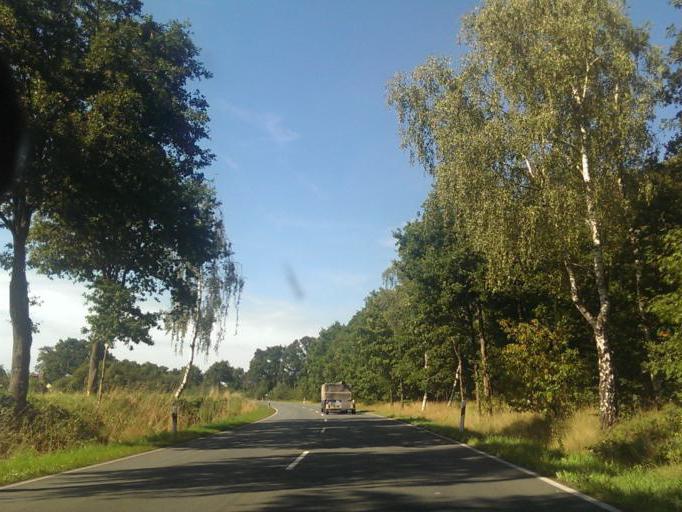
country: DE
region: North Rhine-Westphalia
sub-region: Regierungsbezirk Detmold
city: Hovelhof
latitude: 51.7906
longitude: 8.6200
